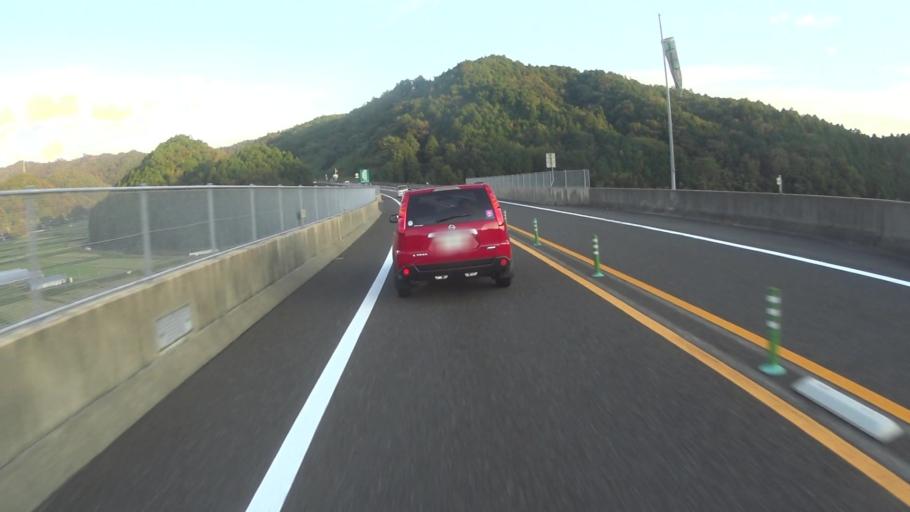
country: JP
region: Kyoto
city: Ayabe
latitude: 35.3857
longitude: 135.2431
